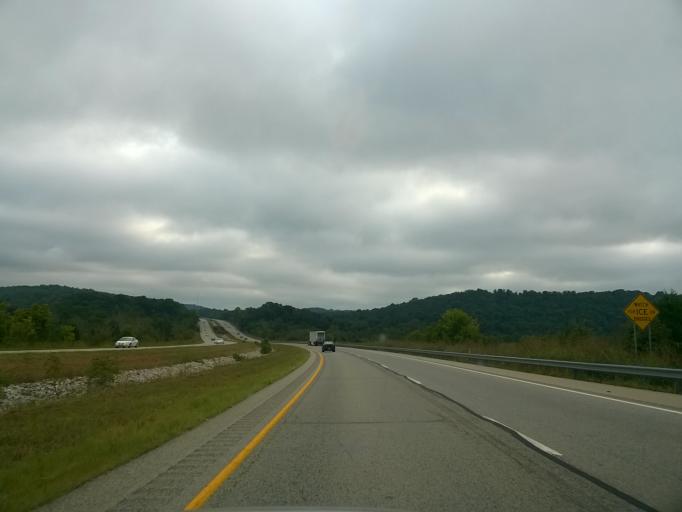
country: US
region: Indiana
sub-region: Harrison County
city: Corydon
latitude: 38.2346
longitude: -86.2322
